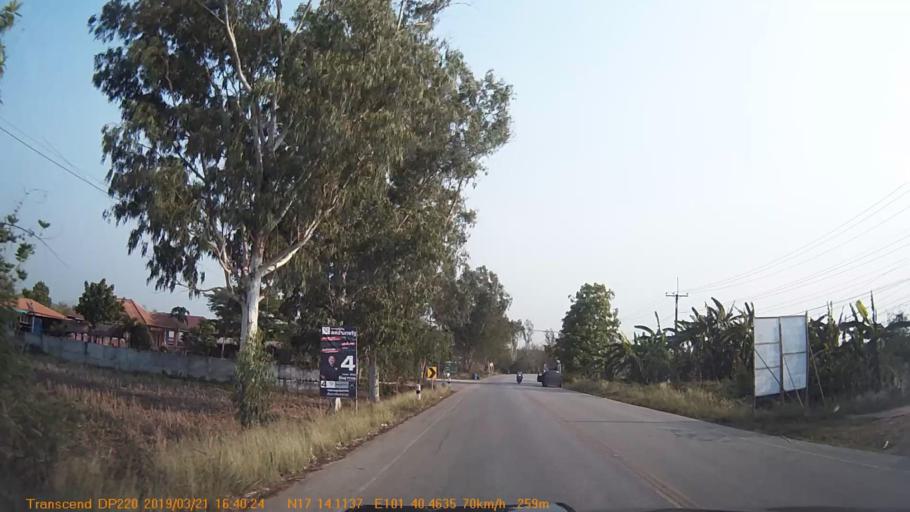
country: TH
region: Loei
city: Phu Luang
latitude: 17.2350
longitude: 101.6744
